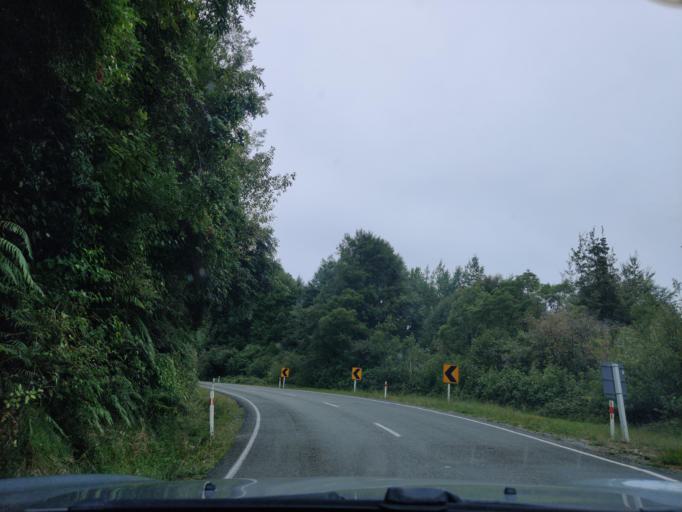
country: NZ
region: West Coast
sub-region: Buller District
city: Westport
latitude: -41.8105
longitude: 172.0899
